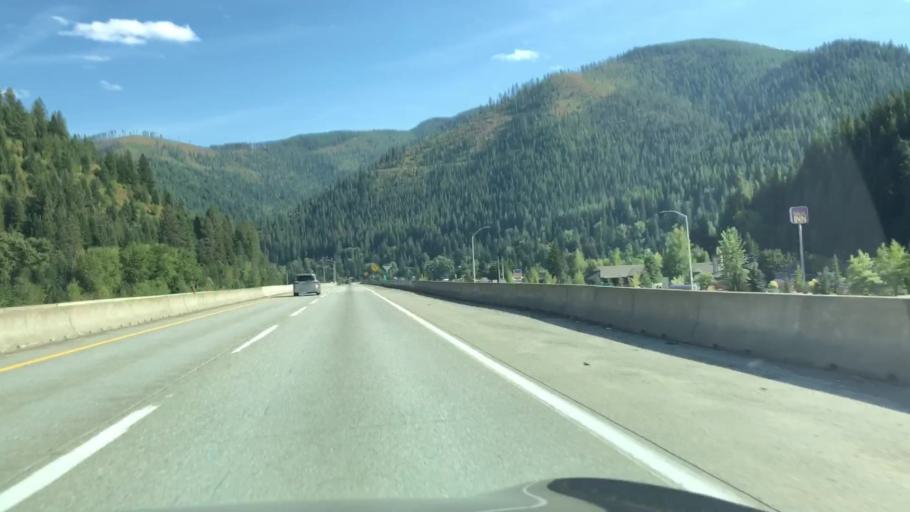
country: US
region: Idaho
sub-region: Shoshone County
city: Wallace
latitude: 47.4789
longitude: -115.9337
